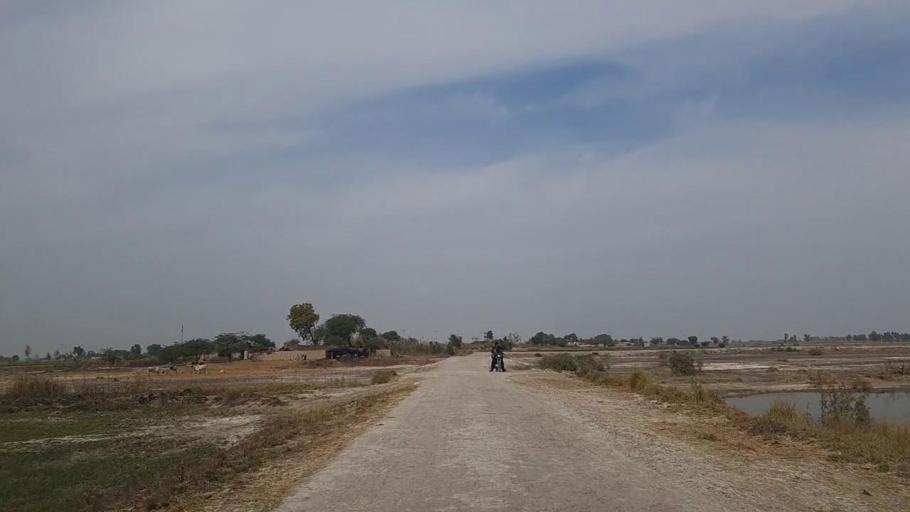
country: PK
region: Sindh
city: Daur
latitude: 26.4769
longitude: 68.4024
